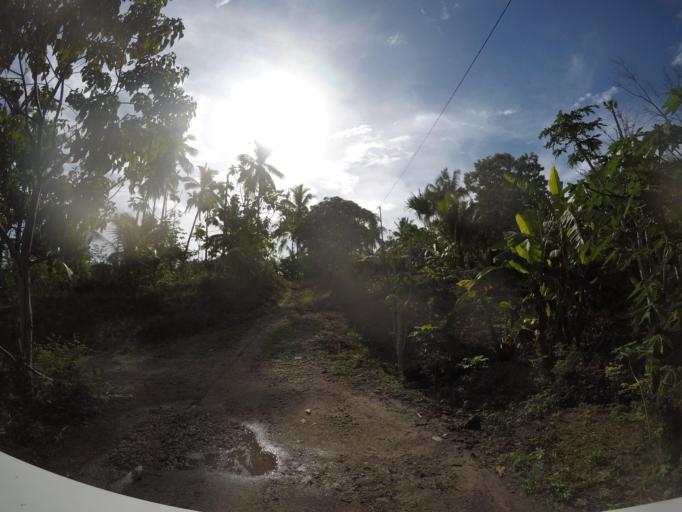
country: TL
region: Baucau
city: Baucau
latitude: -8.5007
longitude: 126.4557
